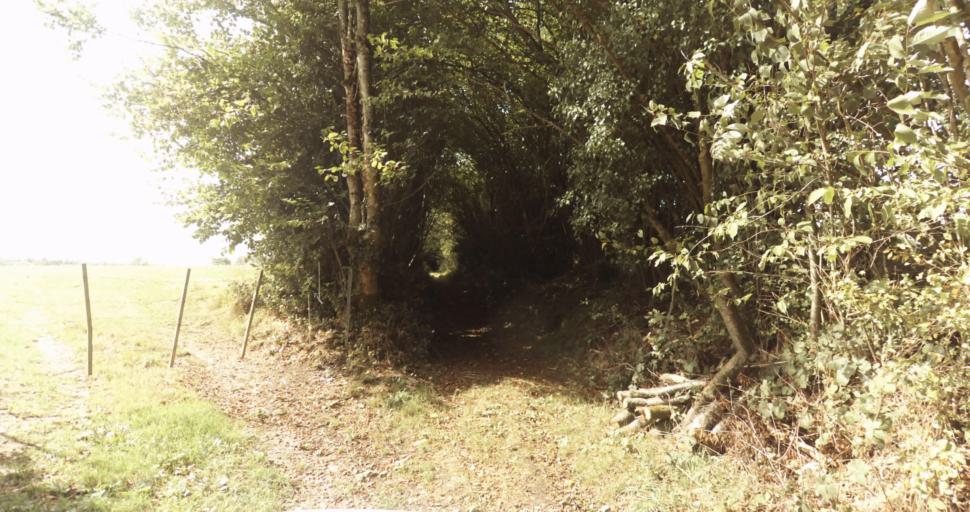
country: FR
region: Lower Normandy
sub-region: Departement de l'Orne
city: Sainte-Gauburge-Sainte-Colombe
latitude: 48.7968
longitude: 0.4034
